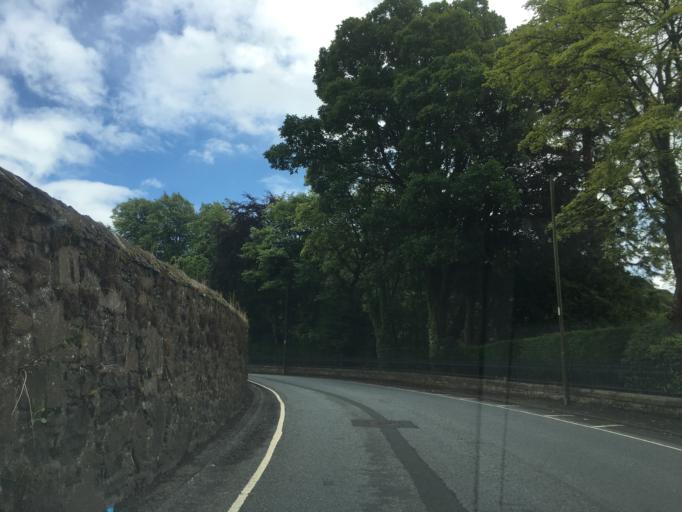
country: GB
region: Scotland
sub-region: Stirling
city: Stirling
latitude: 56.1402
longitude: -3.9222
